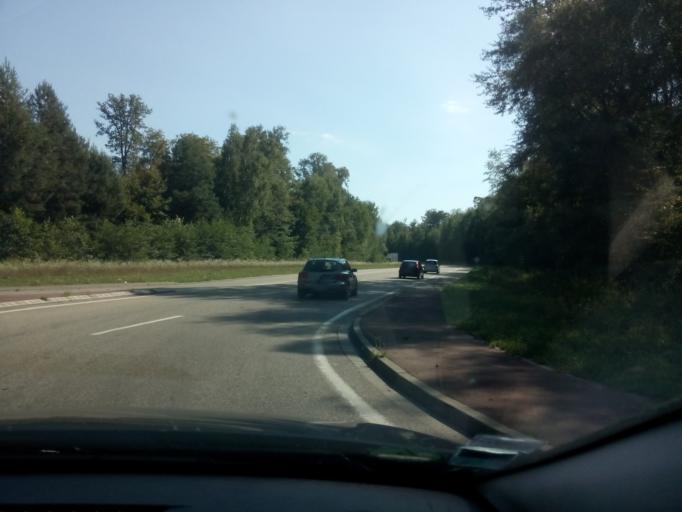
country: FR
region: Alsace
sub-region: Departement du Bas-Rhin
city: Surbourg
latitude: 48.8799
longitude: 7.8252
